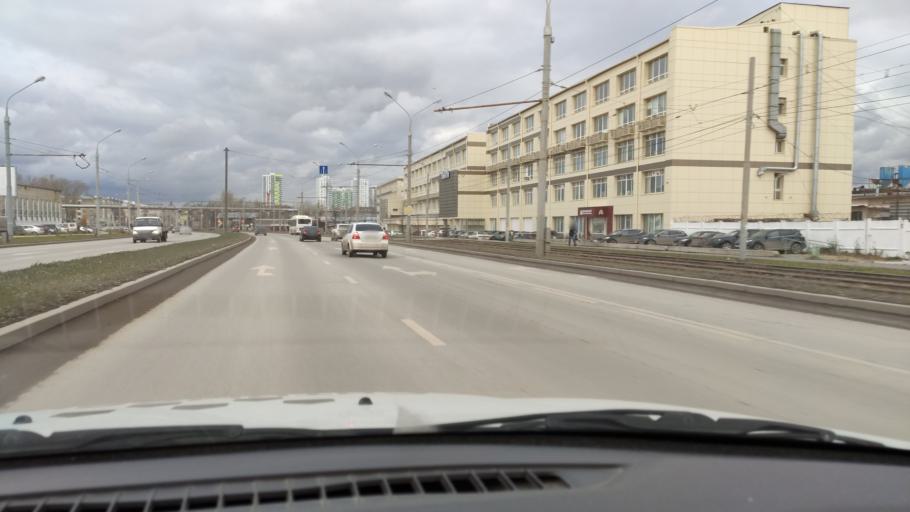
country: RU
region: Perm
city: Perm
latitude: 57.9808
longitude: 56.2599
